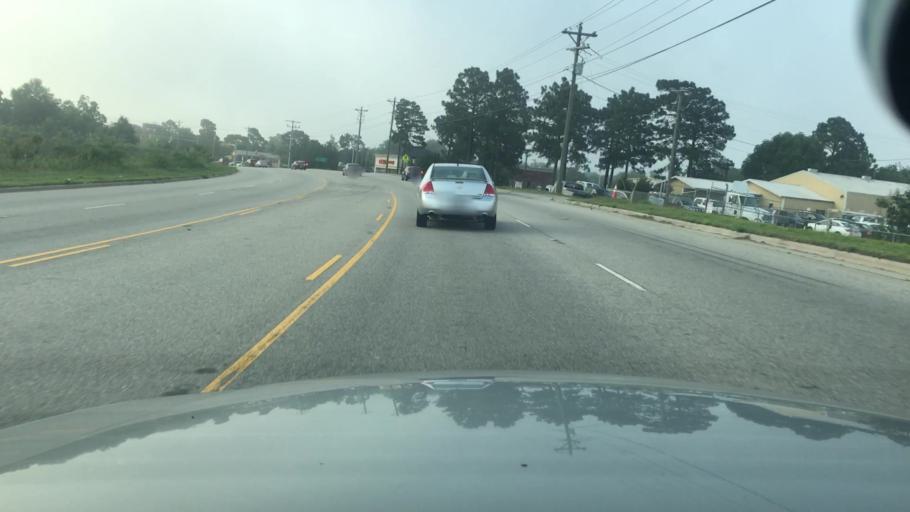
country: US
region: North Carolina
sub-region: Cumberland County
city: Hope Mills
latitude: 35.0055
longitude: -78.9183
